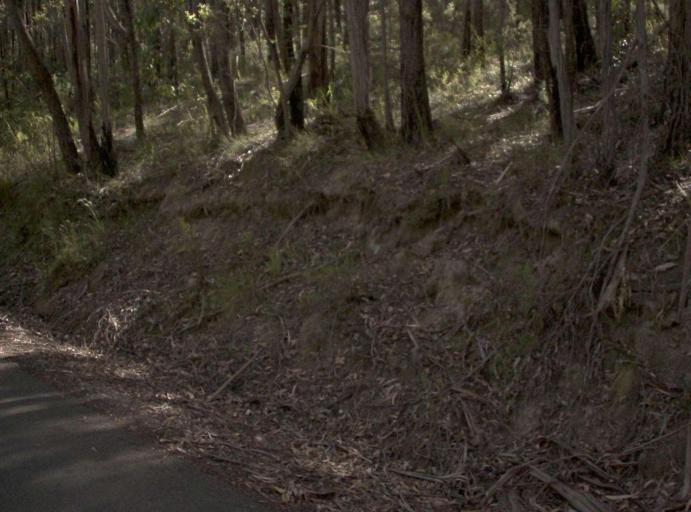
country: AU
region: Victoria
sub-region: East Gippsland
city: Lakes Entrance
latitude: -37.4486
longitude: 148.1269
